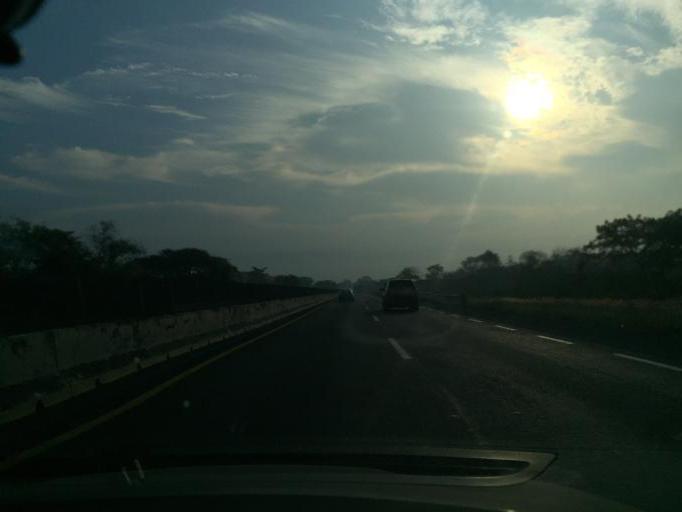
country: MX
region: Veracruz
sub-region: Tierra Blanca
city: Huixcolotla
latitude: 18.7833
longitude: -96.4910
